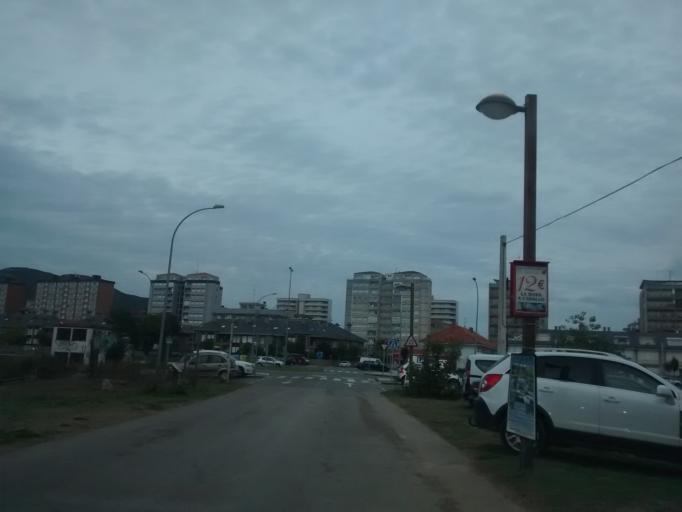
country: ES
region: Cantabria
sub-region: Provincia de Cantabria
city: Colindres
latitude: 43.4167
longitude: -3.4458
